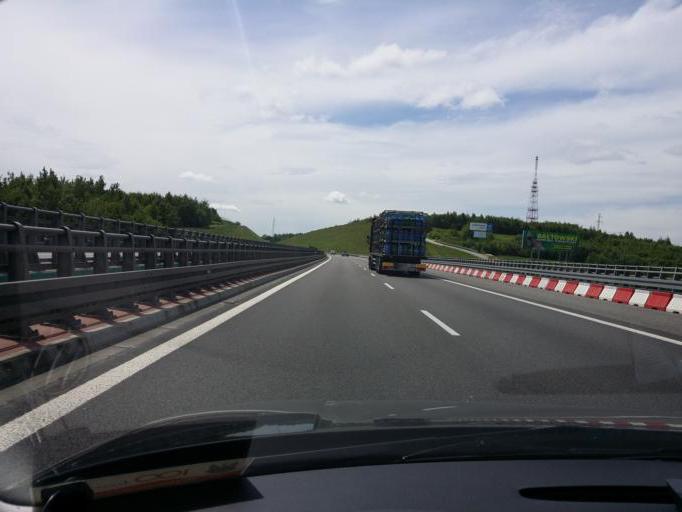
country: PL
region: Swietokrzyskie
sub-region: Powiat skarzyski
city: Laczna
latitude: 50.9848
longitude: 20.7576
